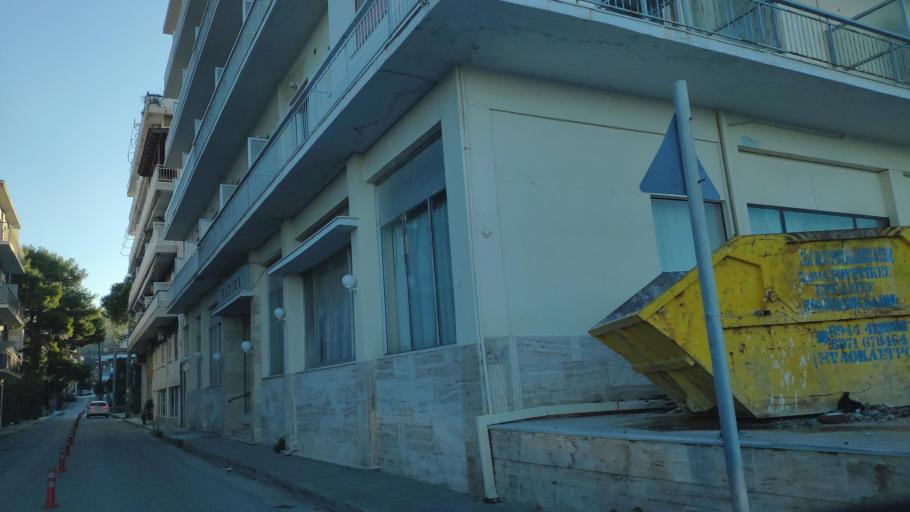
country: GR
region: Peloponnese
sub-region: Nomos Korinthias
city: Xylokastro
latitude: 38.0779
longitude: 22.6380
